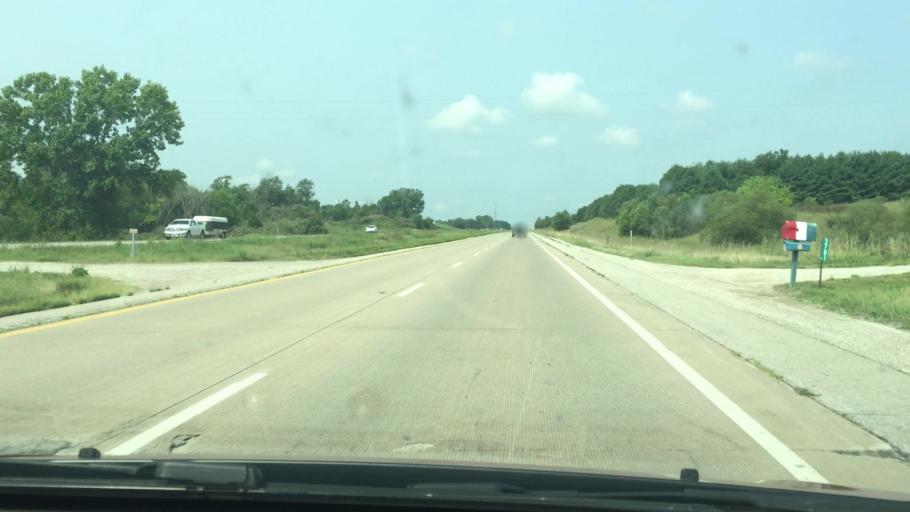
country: US
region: Iowa
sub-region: Scott County
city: Blue Grass
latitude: 41.5158
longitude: -90.8267
